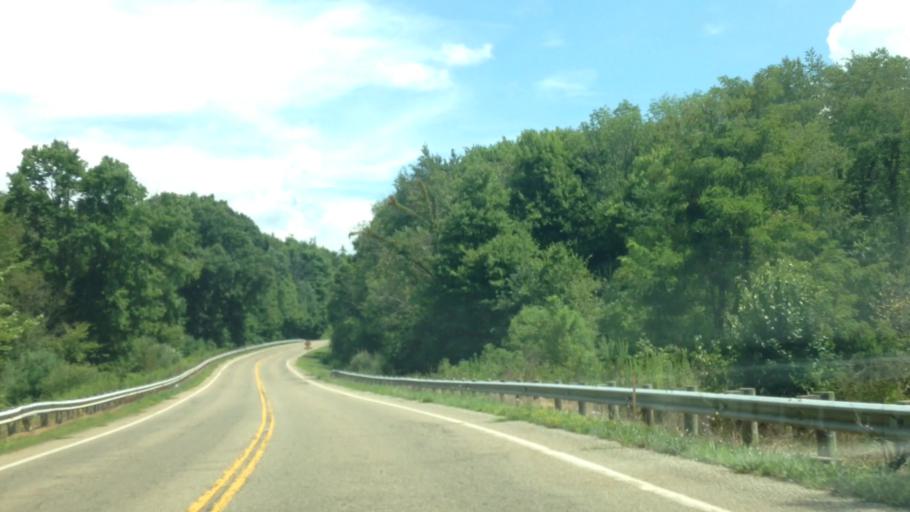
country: US
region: Ohio
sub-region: Summit County
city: Clinton
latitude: 40.9480
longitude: -81.6271
